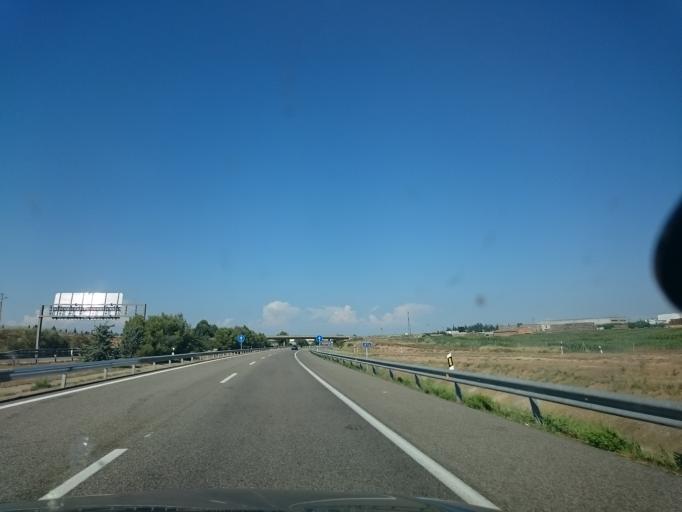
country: ES
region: Catalonia
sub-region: Provincia de Lleida
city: Soses
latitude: 41.5367
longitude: 0.4766
